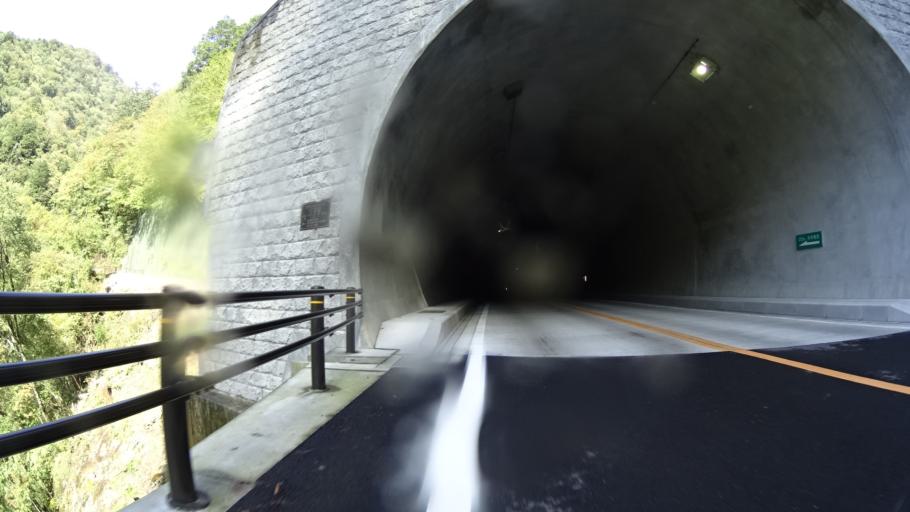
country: JP
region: Yamanashi
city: Enzan
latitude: 35.7996
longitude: 138.8652
